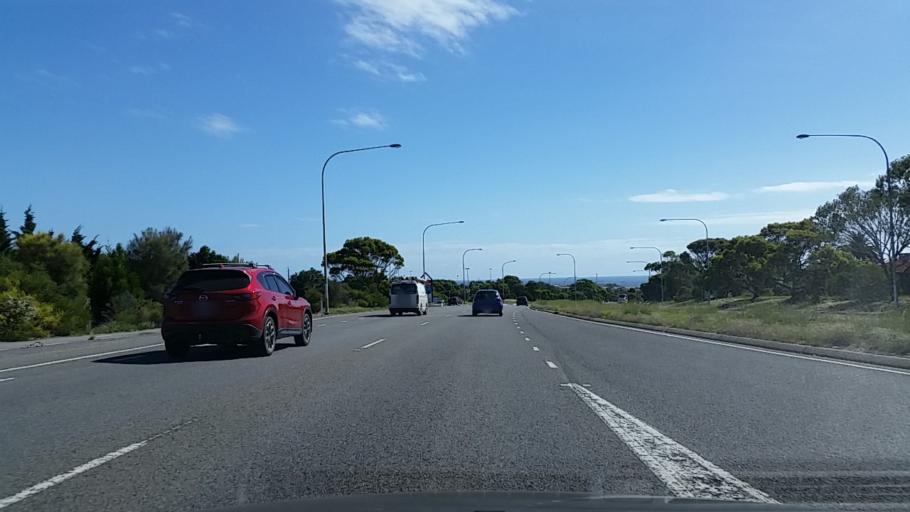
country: AU
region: South Australia
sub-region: Onkaparinga
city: Reynella
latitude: -35.0840
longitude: 138.5102
